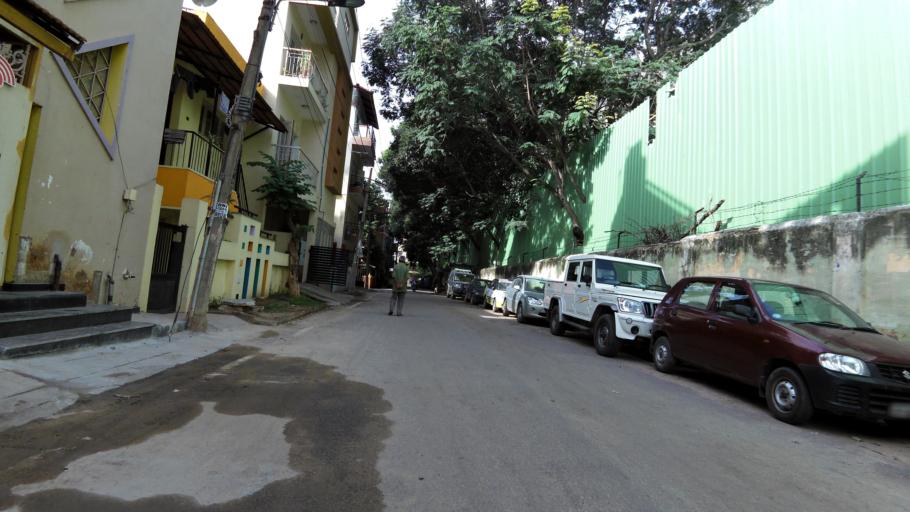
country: IN
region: Karnataka
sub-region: Bangalore Urban
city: Bangalore
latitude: 12.9988
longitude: 77.6293
